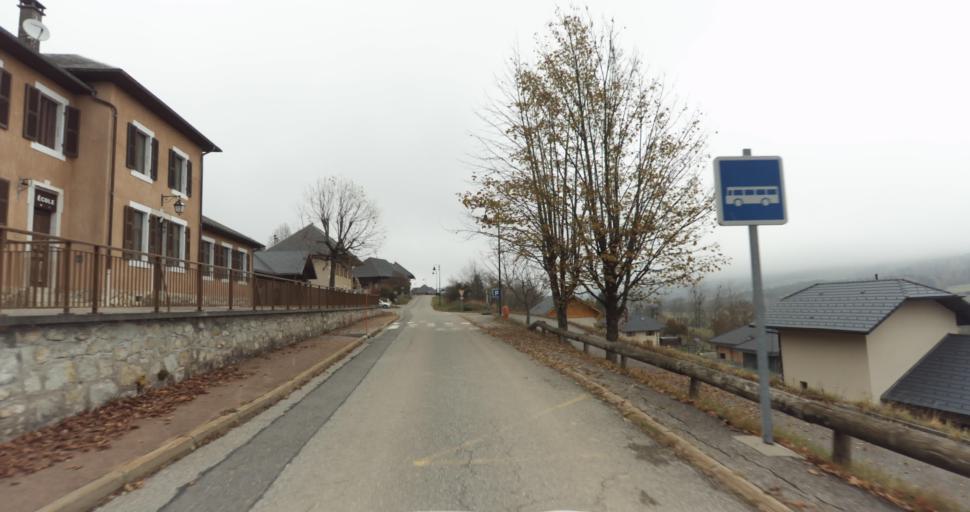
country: FR
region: Rhone-Alpes
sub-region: Departement de la Haute-Savoie
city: Gruffy
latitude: 45.7707
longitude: 6.1242
